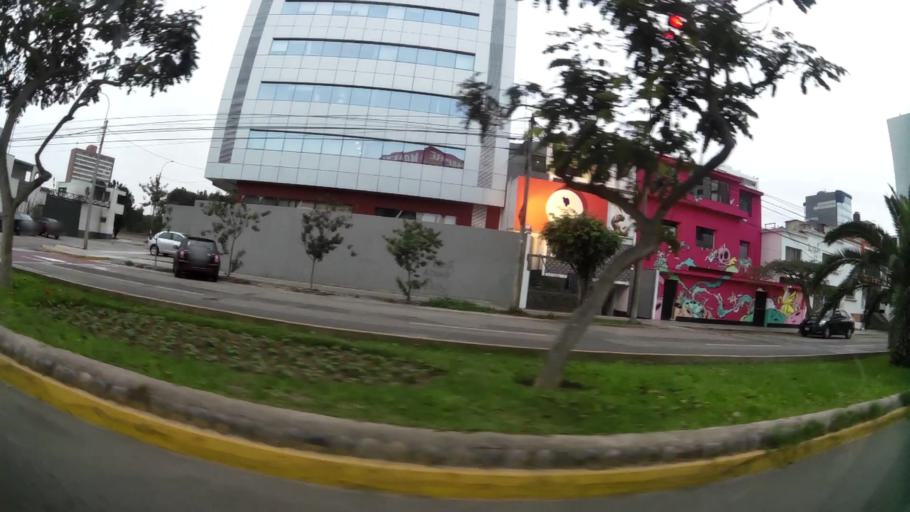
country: PE
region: Lima
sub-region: Lima
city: Surco
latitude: -12.1279
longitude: -77.0241
